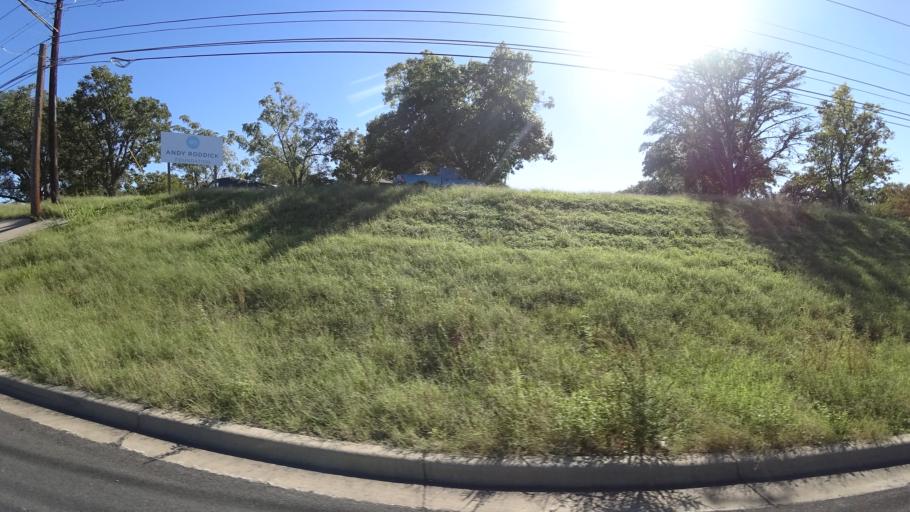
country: US
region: Texas
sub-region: Travis County
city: Hornsby Bend
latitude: 30.2778
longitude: -97.6394
